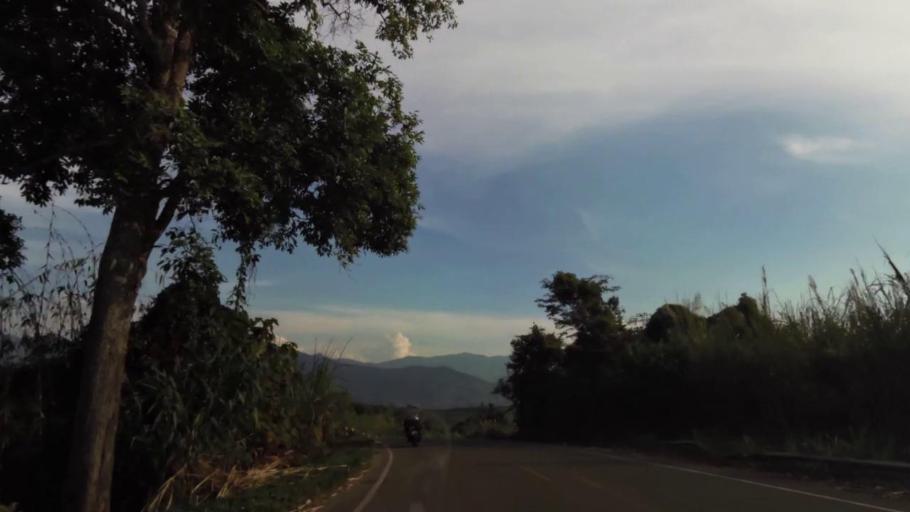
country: TH
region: Chiang Rai
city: Khun Tan
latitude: 19.8621
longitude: 100.3670
